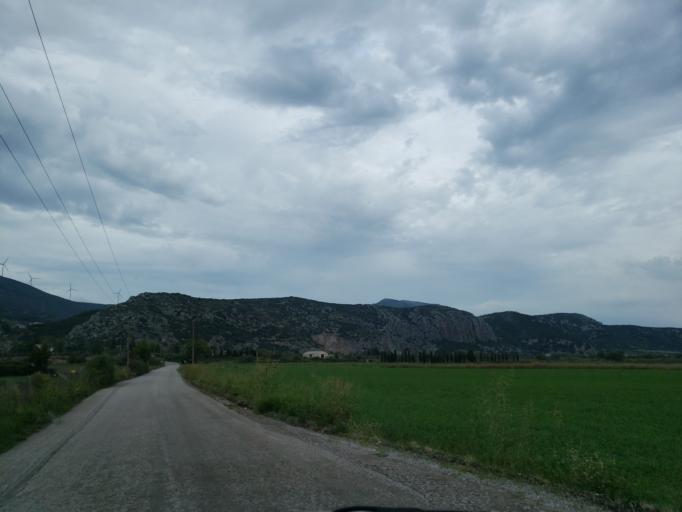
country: GR
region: Central Greece
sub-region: Nomos Voiotias
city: Akraifnia
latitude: 38.4452
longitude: 23.2059
